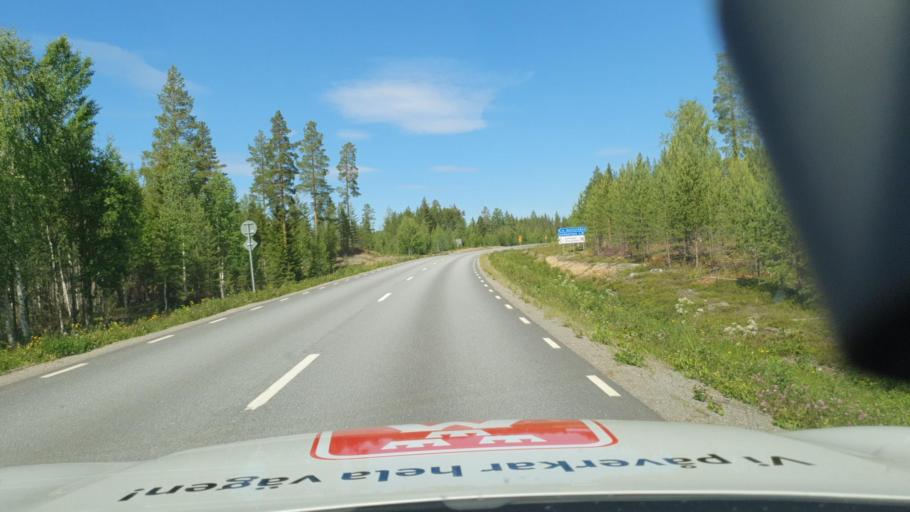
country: SE
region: Vaesterbotten
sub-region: Skelleftea Kommun
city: Langsele
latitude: 64.7526
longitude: 20.3426
